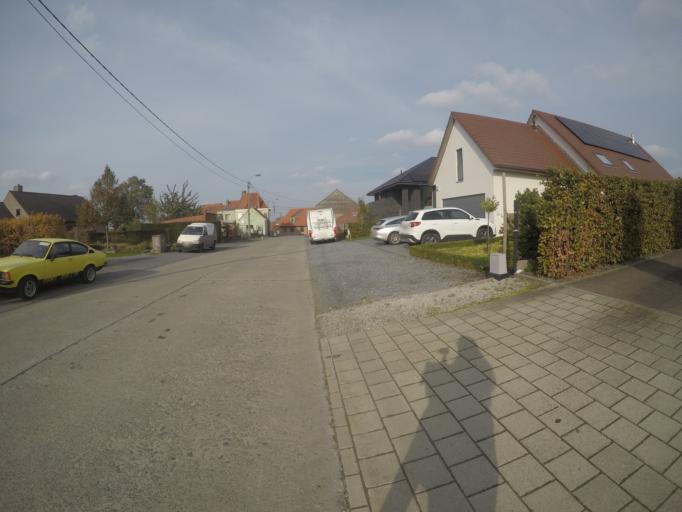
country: BE
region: Flanders
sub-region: Provincie West-Vlaanderen
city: Moorslede
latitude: 50.8417
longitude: 3.0591
